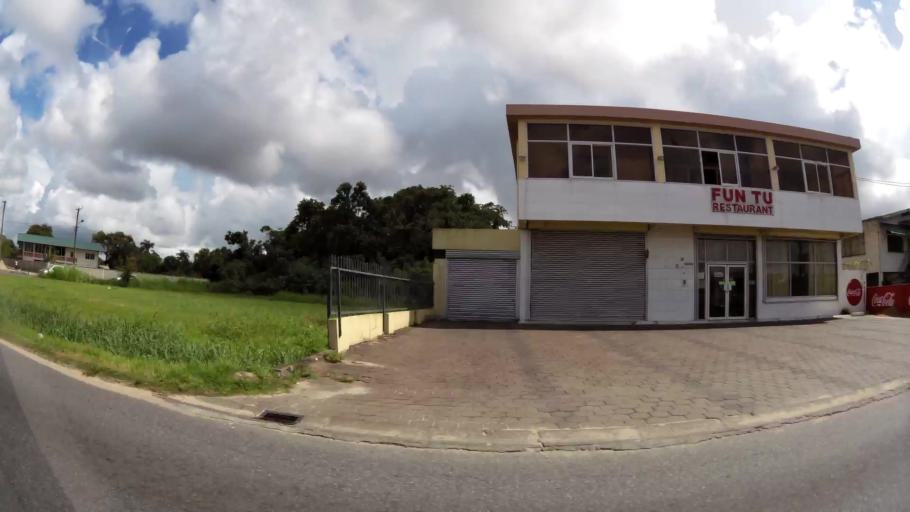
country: SR
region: Paramaribo
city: Paramaribo
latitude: 5.8321
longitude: -55.1923
